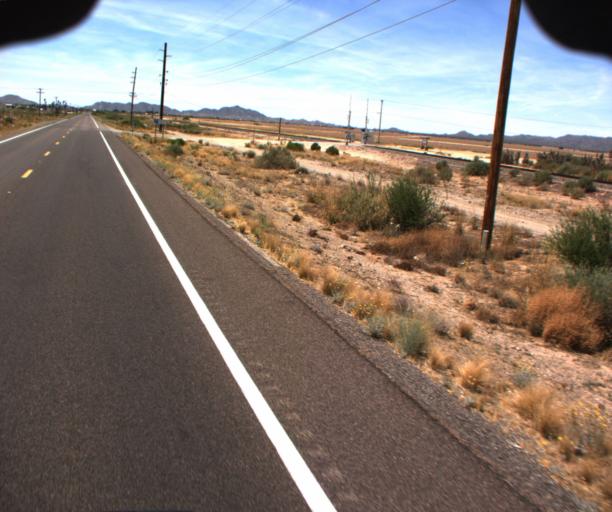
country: US
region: Arizona
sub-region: La Paz County
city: Salome
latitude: 33.7948
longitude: -113.5912
